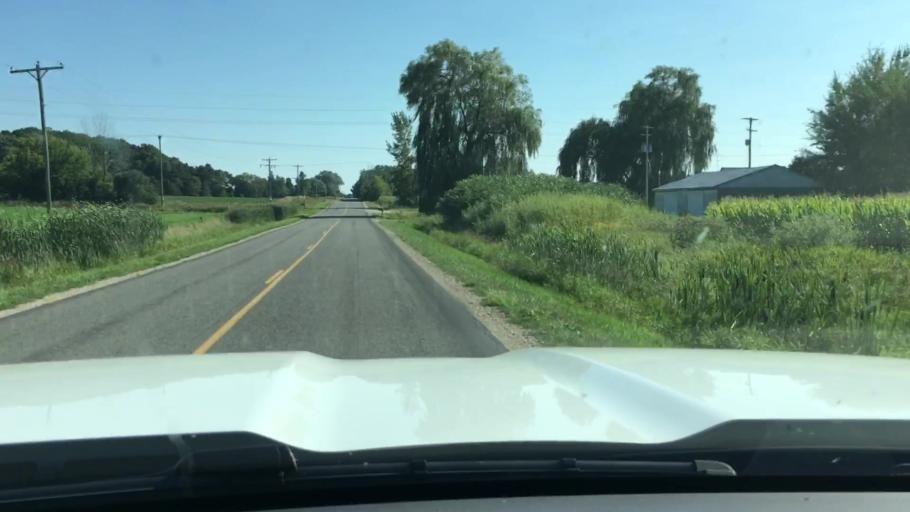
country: US
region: Michigan
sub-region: Muskegon County
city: Ravenna
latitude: 43.2513
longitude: -85.9180
